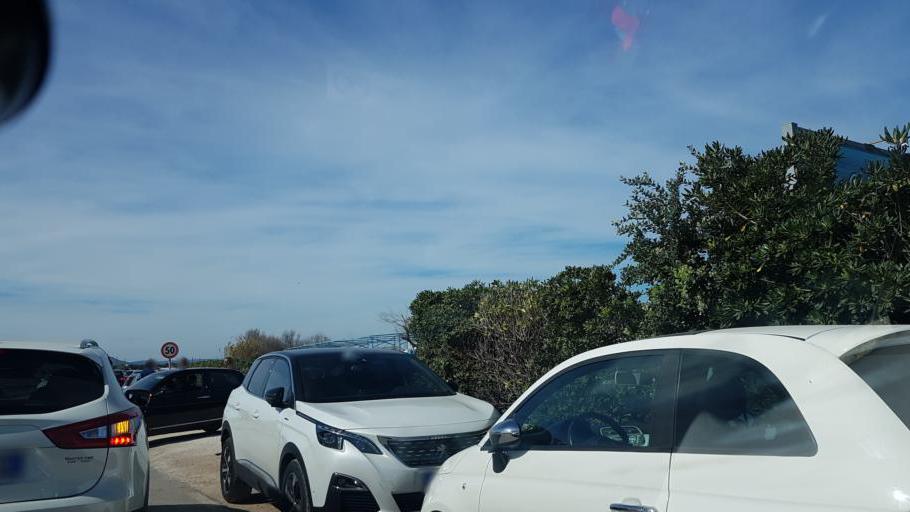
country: IT
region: Apulia
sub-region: Provincia di Brindisi
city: Pezze di Greco
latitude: 40.8567
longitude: 17.4375
